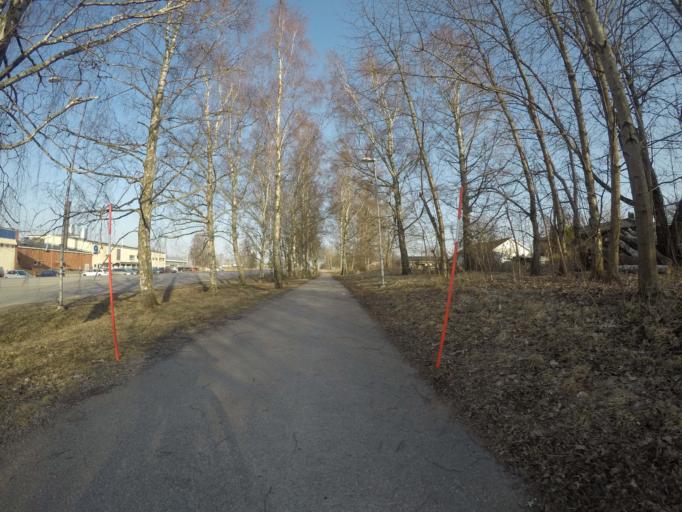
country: SE
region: Vaestmanland
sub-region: Kungsors Kommun
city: Kungsoer
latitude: 59.4253
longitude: 16.1212
